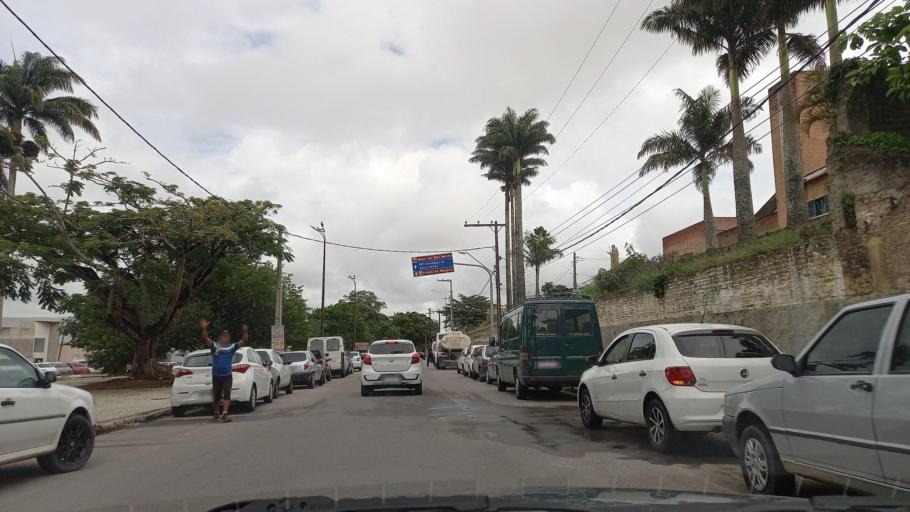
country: BR
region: Pernambuco
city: Garanhuns
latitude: -8.8882
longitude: -36.4937
